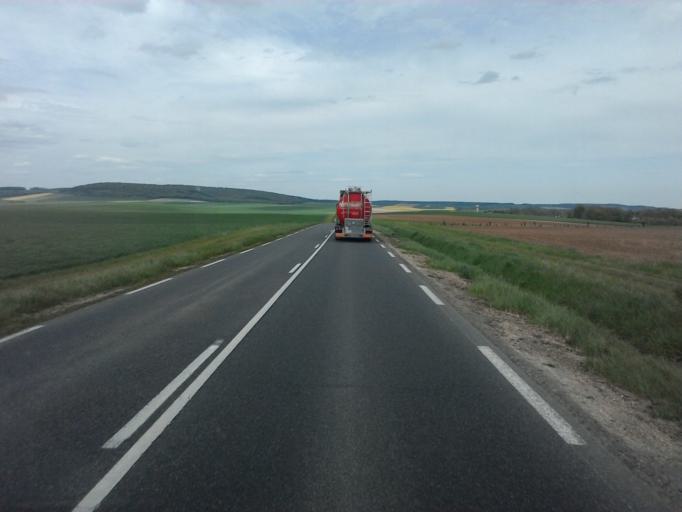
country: FR
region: Bourgogne
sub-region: Departement de l'Yonne
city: Neuvy-Sautour
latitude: 48.0544
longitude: 3.8001
